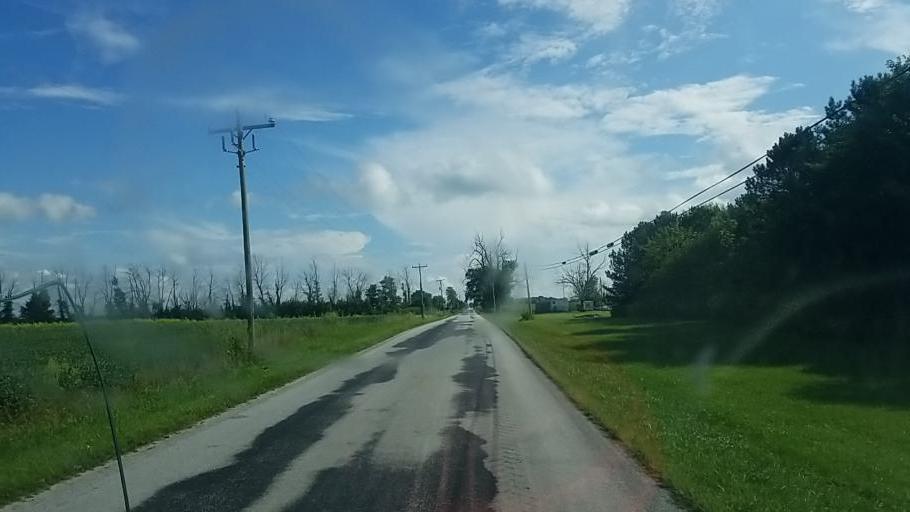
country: US
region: Ohio
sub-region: Hardin County
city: Kenton
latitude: 40.6753
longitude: -83.5380
